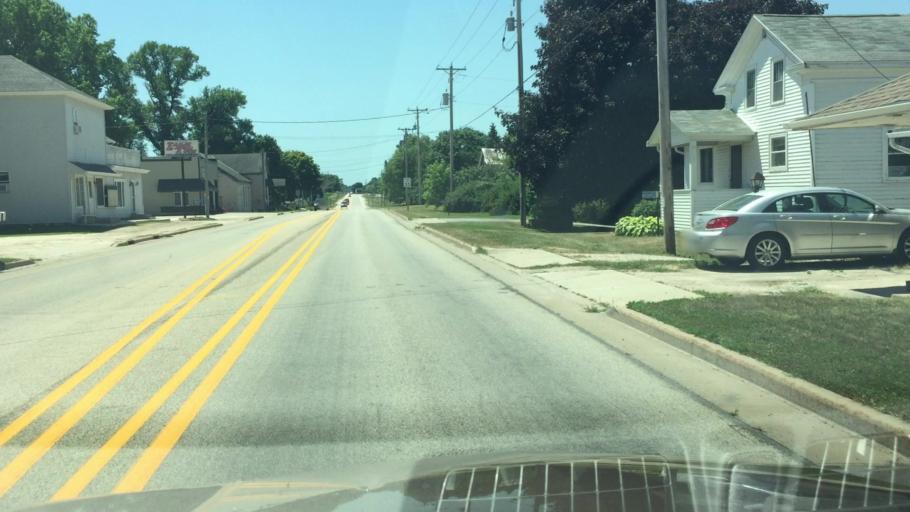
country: US
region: Wisconsin
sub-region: Fond du Lac County
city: Saint Peter
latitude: 43.9357
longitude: -88.3035
